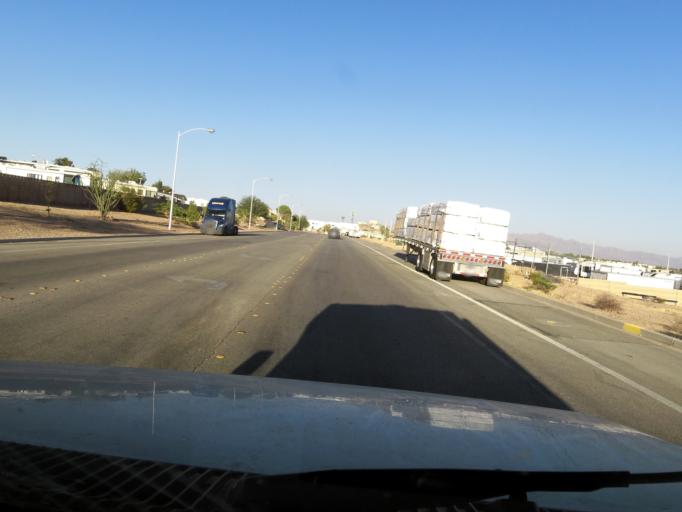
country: US
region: Nevada
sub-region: Clark County
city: Boulder City
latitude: 35.9759
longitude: -114.8522
